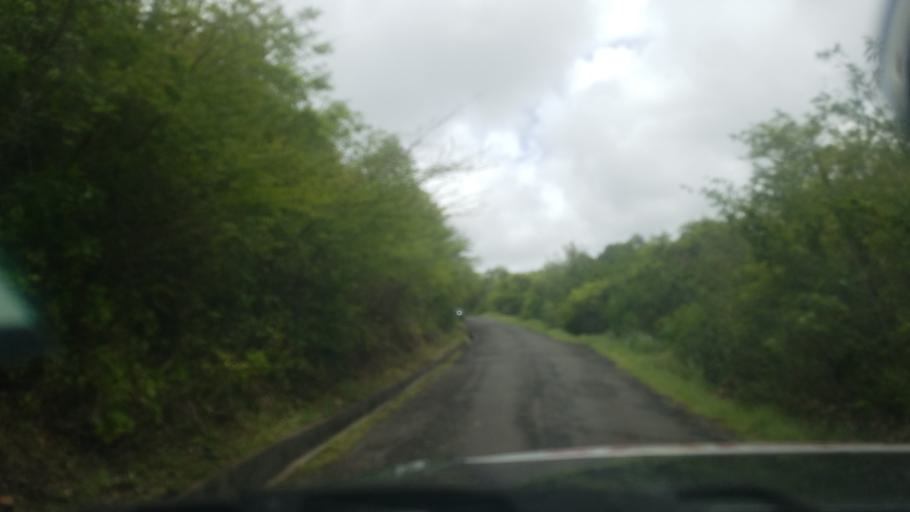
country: LC
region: Laborie Quarter
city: Laborie
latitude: 13.7440
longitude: -60.9638
